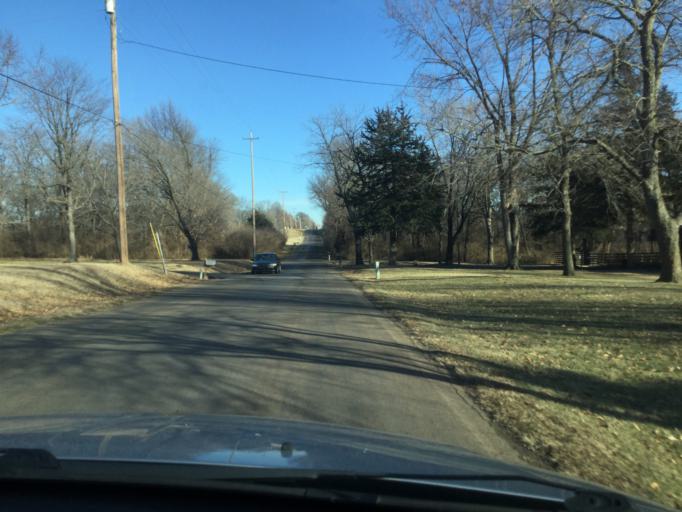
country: US
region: Kansas
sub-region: Shawnee County
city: Topeka
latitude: 39.1167
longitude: -95.6798
